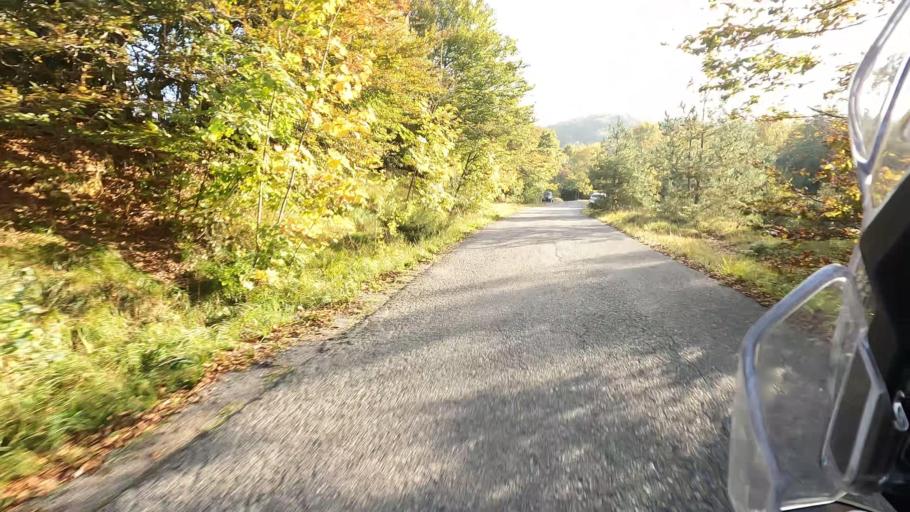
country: IT
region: Liguria
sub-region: Provincia di Savona
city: Urbe
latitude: 44.4449
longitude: 8.5789
